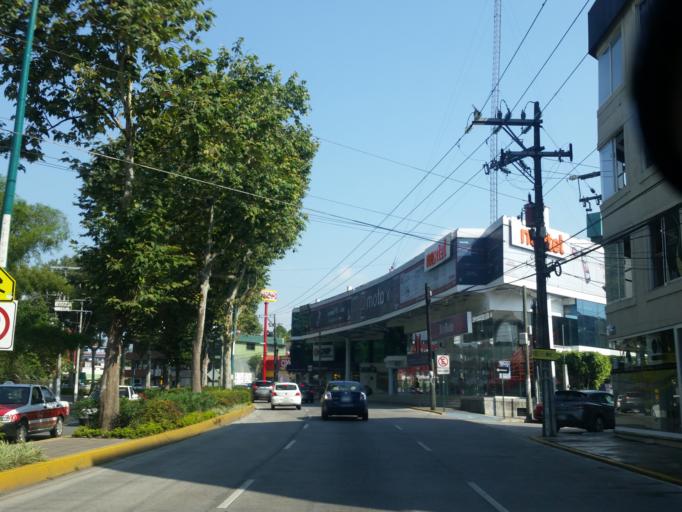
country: MX
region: Veracruz
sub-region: Xalapa
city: Xalapa de Enriquez
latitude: 19.5210
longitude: -96.9059
